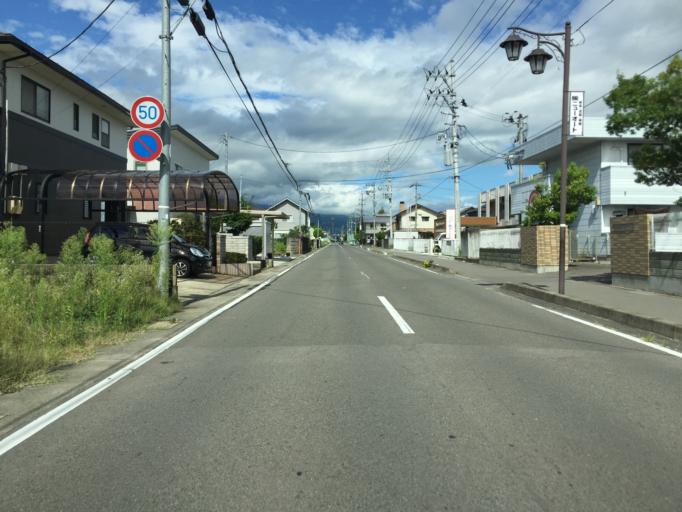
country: JP
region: Fukushima
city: Fukushima-shi
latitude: 37.7250
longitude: 140.4453
